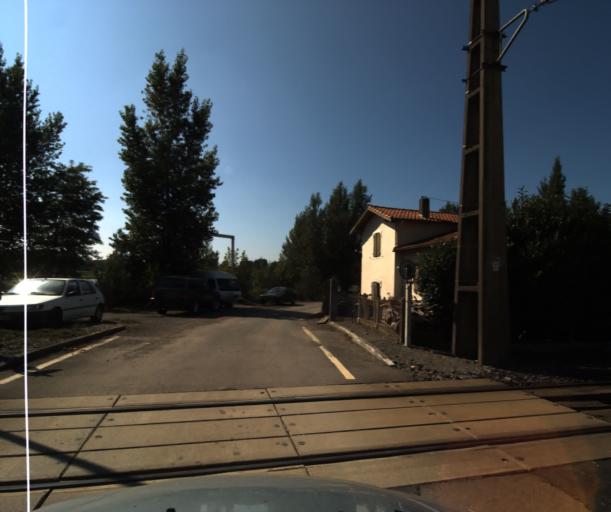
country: FR
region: Midi-Pyrenees
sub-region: Departement de la Haute-Garonne
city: Noe
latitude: 43.3719
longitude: 1.2613
